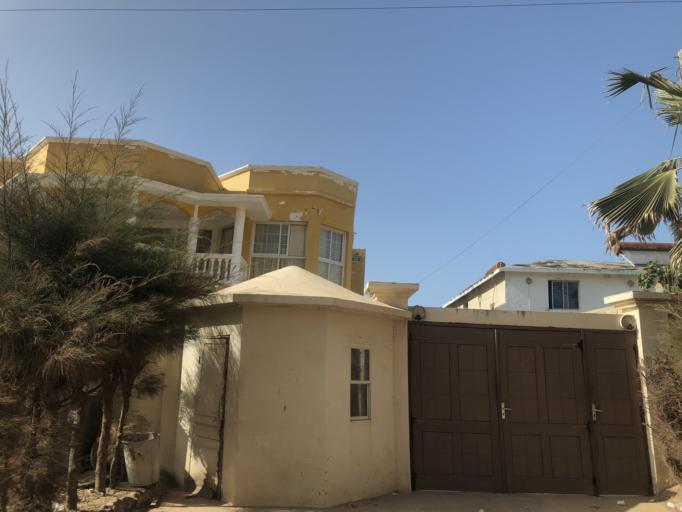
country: SN
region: Dakar
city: Mermoz Boabab
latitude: 14.7548
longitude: -17.4941
